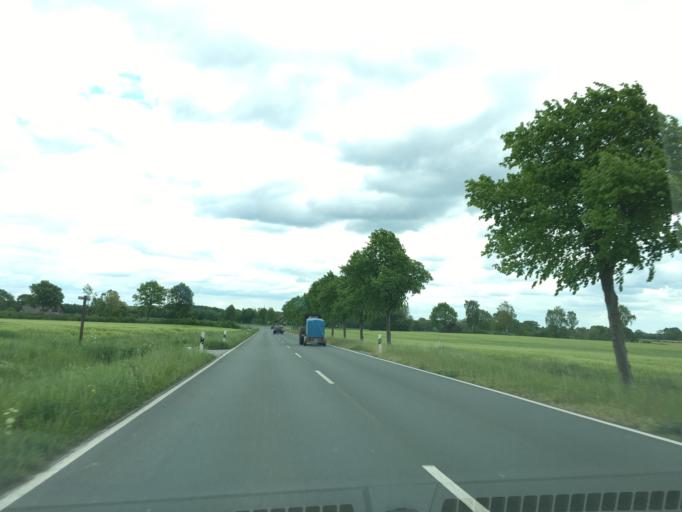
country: DE
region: North Rhine-Westphalia
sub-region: Regierungsbezirk Munster
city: Havixbeck
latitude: 51.9243
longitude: 7.4600
